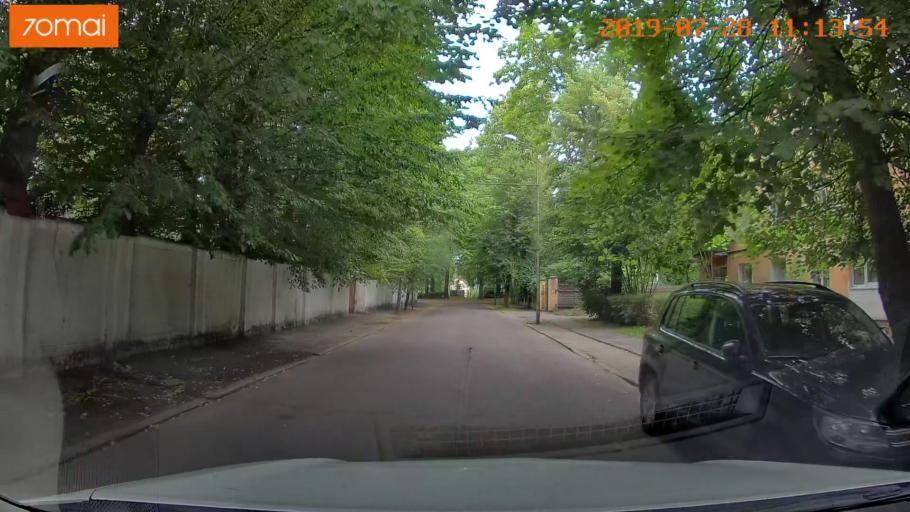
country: RU
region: Kaliningrad
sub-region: Gorod Kaliningrad
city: Kaliningrad
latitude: 54.7187
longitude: 20.4704
